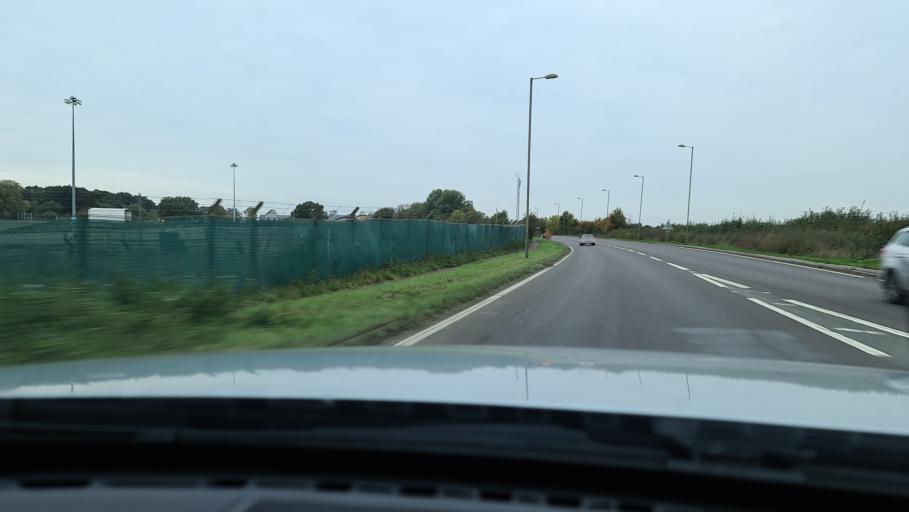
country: GB
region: England
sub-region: Oxfordshire
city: Bicester
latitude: 51.8831
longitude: -1.1359
